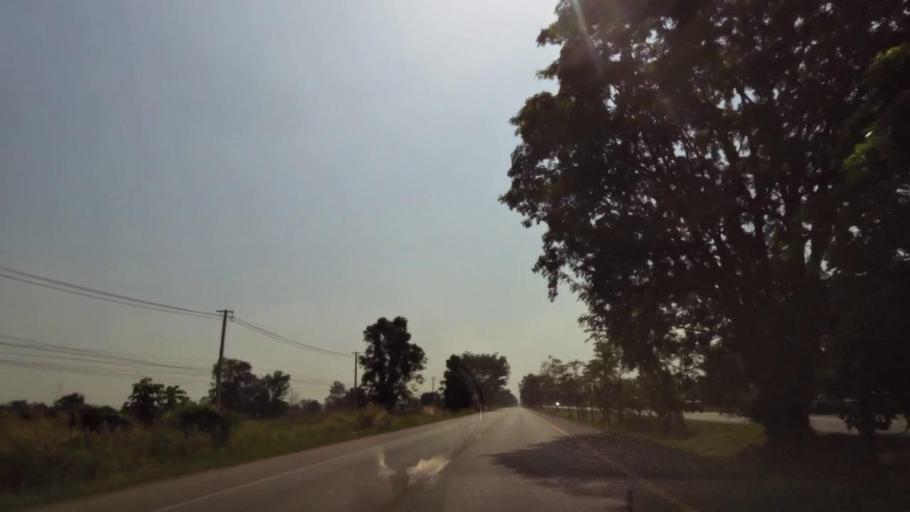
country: TH
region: Phichit
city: Bueng Na Rang
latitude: 16.2900
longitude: 100.1281
